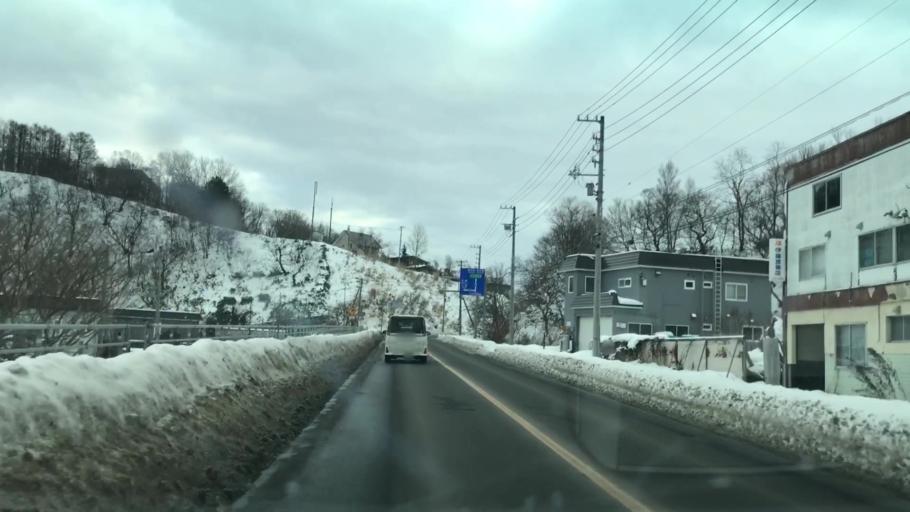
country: JP
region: Hokkaido
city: Yoichi
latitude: 43.1982
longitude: 140.7835
